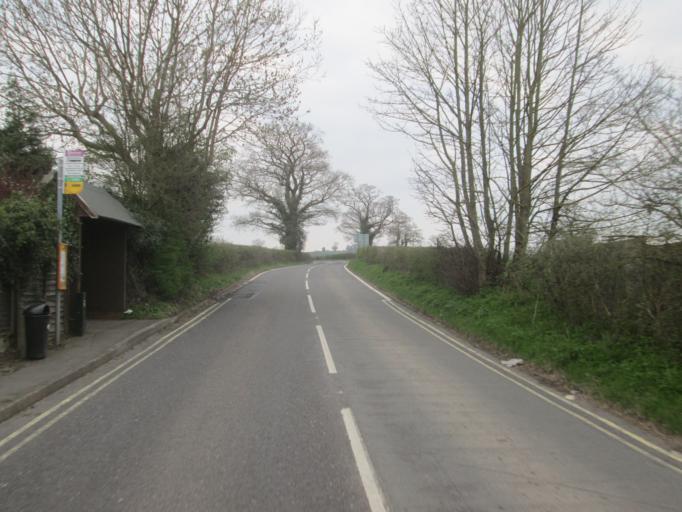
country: GB
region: England
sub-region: Derbyshire
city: Belper
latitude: 53.0193
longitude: -1.5447
